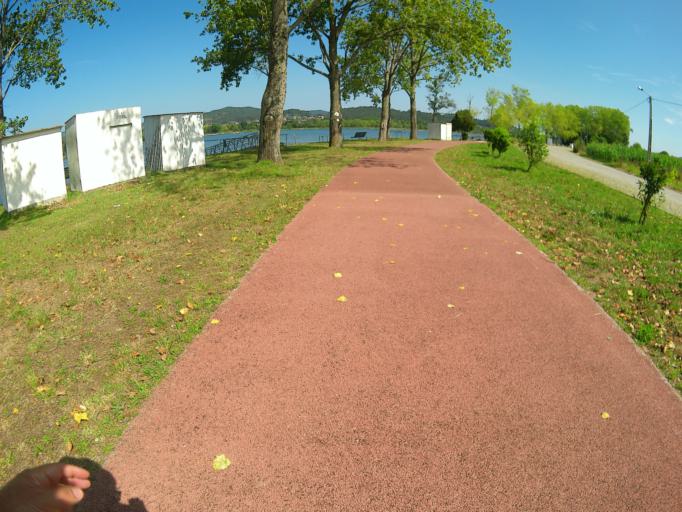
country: ES
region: Galicia
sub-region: Provincia de Pontevedra
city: O Rosal
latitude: 41.9114
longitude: -8.7932
